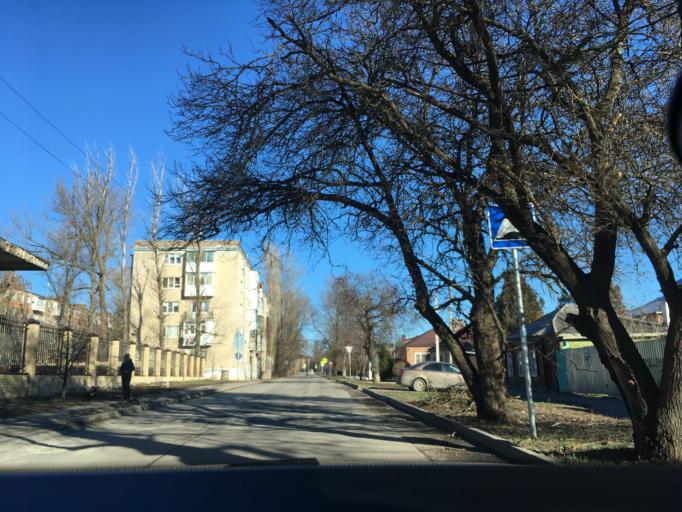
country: RU
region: Rostov
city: Imeni Chkalova
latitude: 47.2681
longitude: 39.7907
